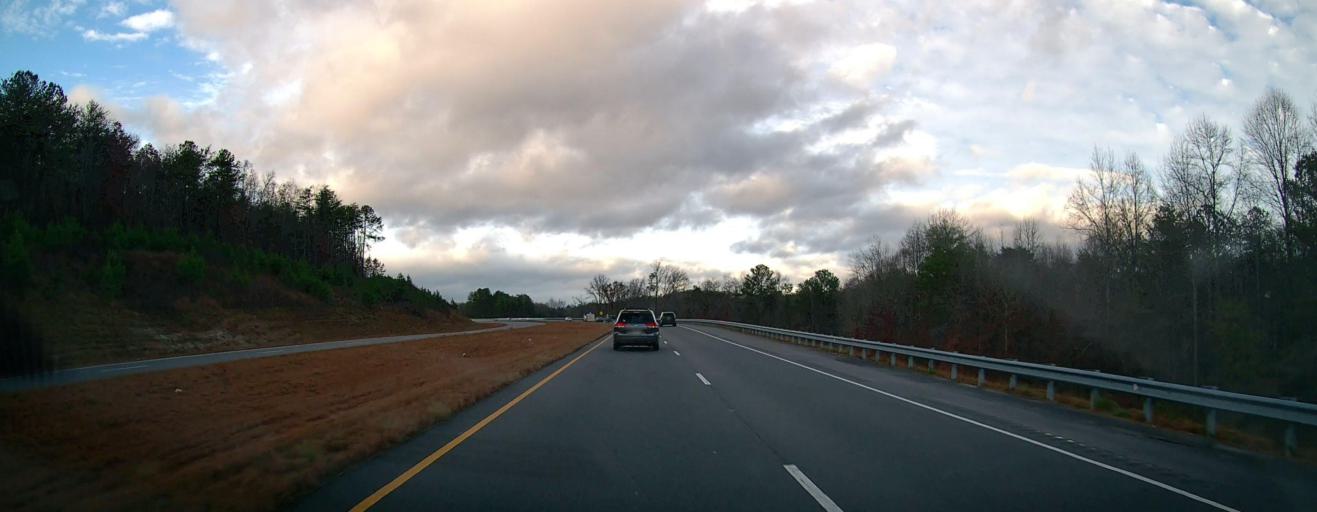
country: US
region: Georgia
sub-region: White County
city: Cleveland
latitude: 34.5962
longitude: -83.7816
